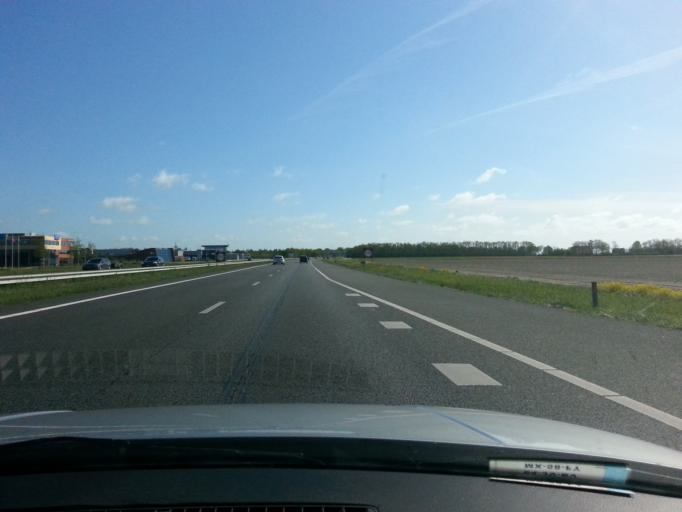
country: NL
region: Flevoland
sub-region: Gemeente Noordoostpolder
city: Emmeloord
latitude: 52.6867
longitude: 5.7513
